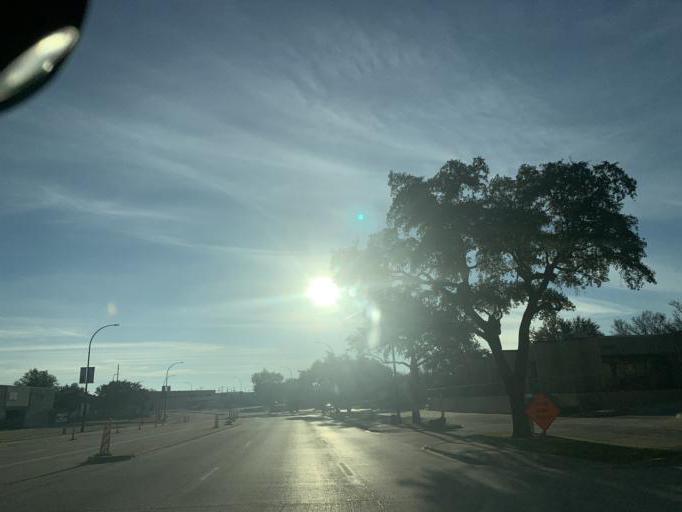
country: US
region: Texas
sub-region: Tarrant County
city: Arlington
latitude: 32.7488
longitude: -97.0781
